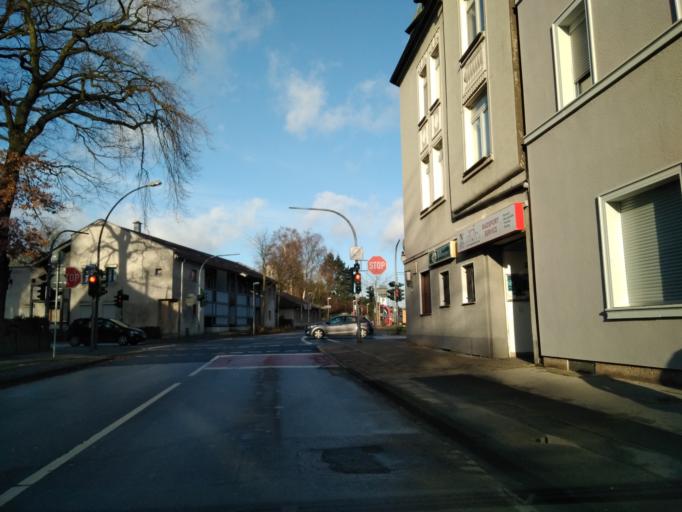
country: DE
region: North Rhine-Westphalia
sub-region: Regierungsbezirk Munster
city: Gladbeck
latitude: 51.5745
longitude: 6.9577
